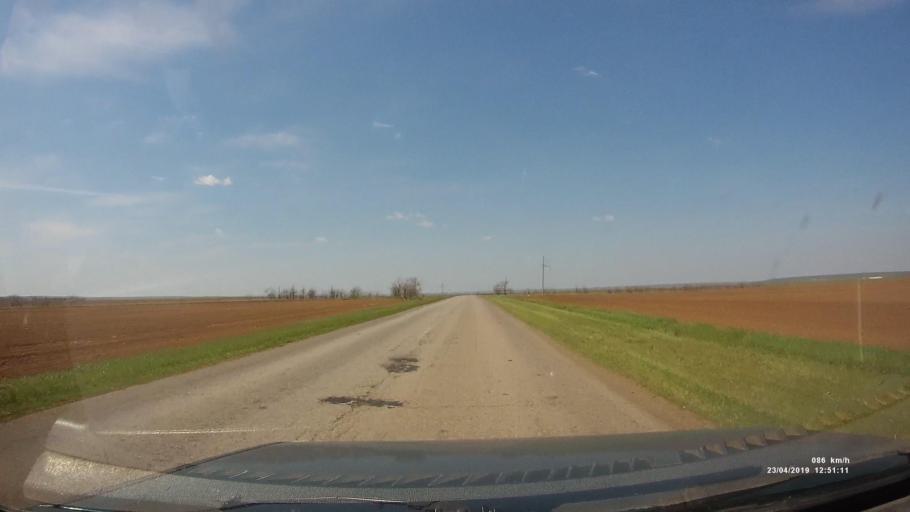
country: RU
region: Kalmykiya
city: Yashalta
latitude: 46.5525
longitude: 42.6261
